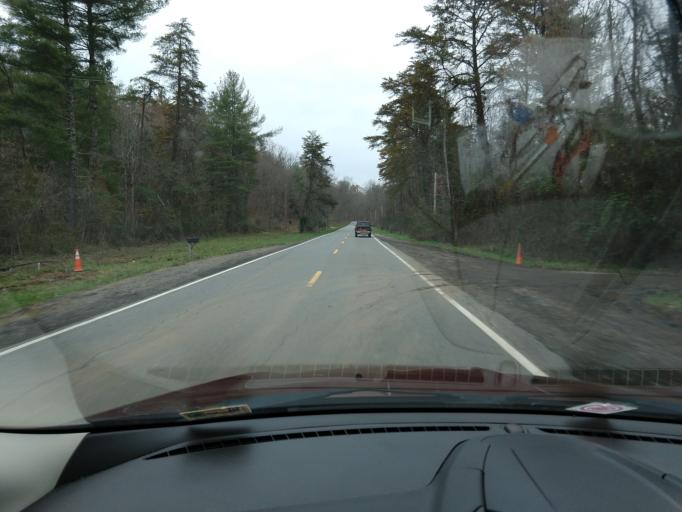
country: US
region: Virginia
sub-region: City of Covington
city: Covington
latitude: 37.7770
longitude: -80.1086
